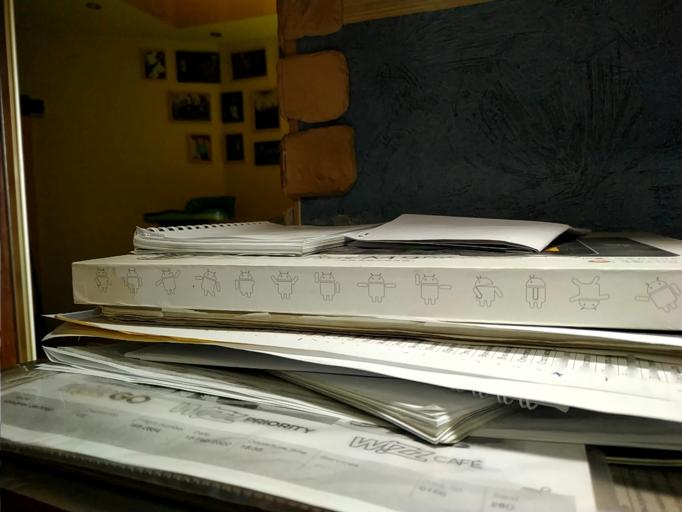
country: RU
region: Novgorod
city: Volot
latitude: 57.6928
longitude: 30.6752
